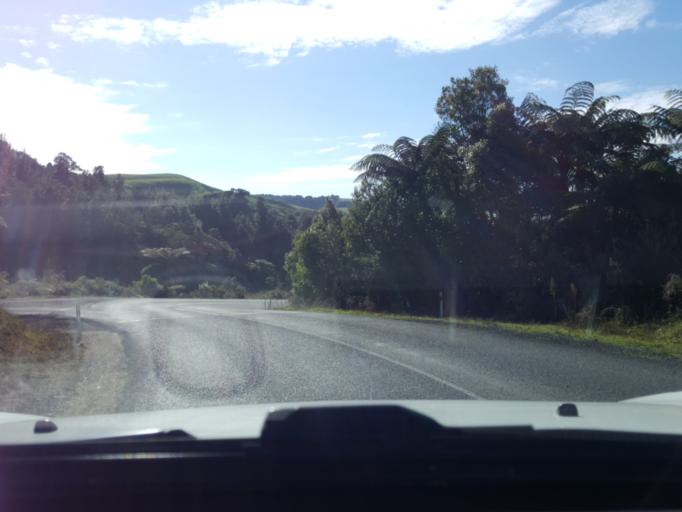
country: NZ
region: Waikato
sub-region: Waikato District
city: Raglan
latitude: -37.9056
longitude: 174.9008
